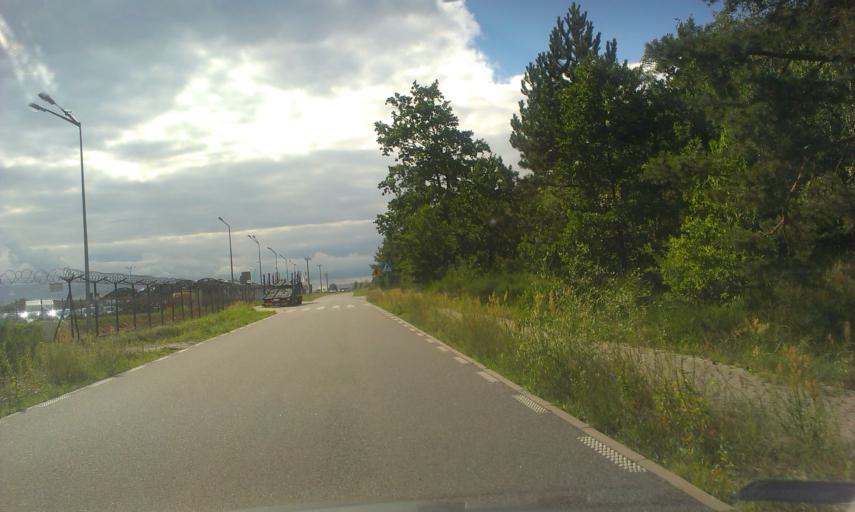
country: PL
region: Masovian Voivodeship
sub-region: Powiat zyrardowski
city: Radziejowice
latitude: 51.9699
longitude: 20.5796
